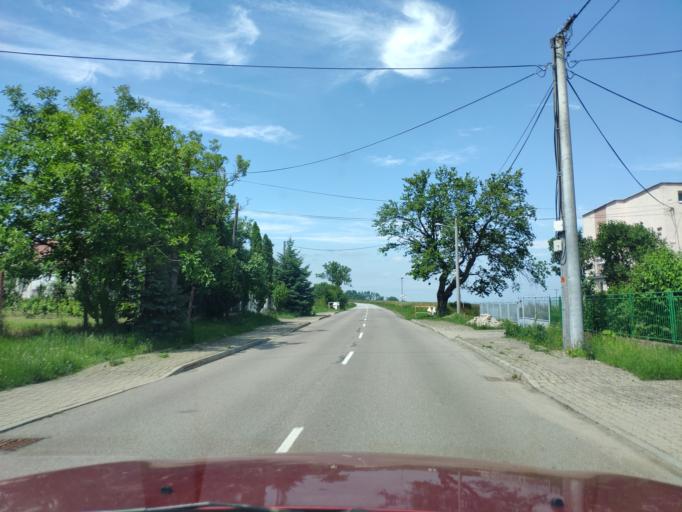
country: SK
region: Kosicky
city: Secovce
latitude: 48.7068
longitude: 21.6542
